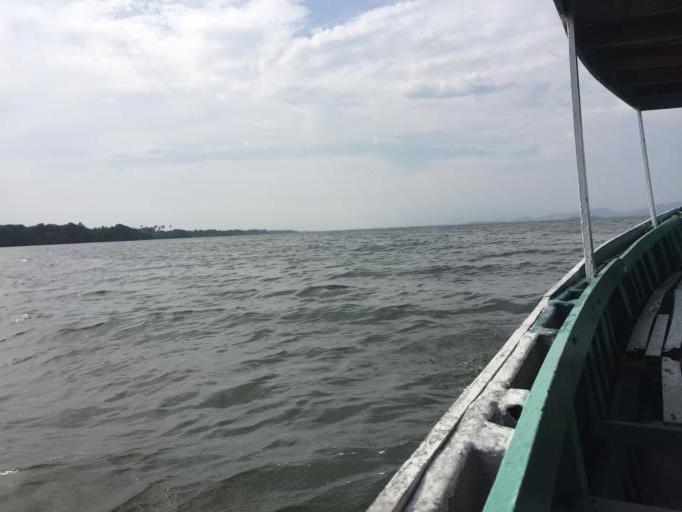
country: MX
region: Guerrero
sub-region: Coyuca de Benitez
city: Colonia Luces en el Mar
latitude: 16.9134
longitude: -99.9786
